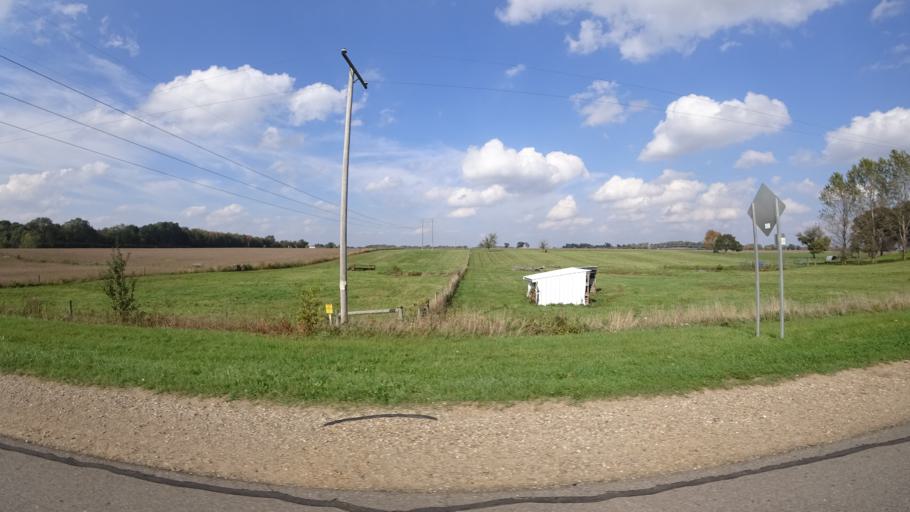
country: US
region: Michigan
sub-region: Saint Joseph County
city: Centreville
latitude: 42.0068
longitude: -85.4391
